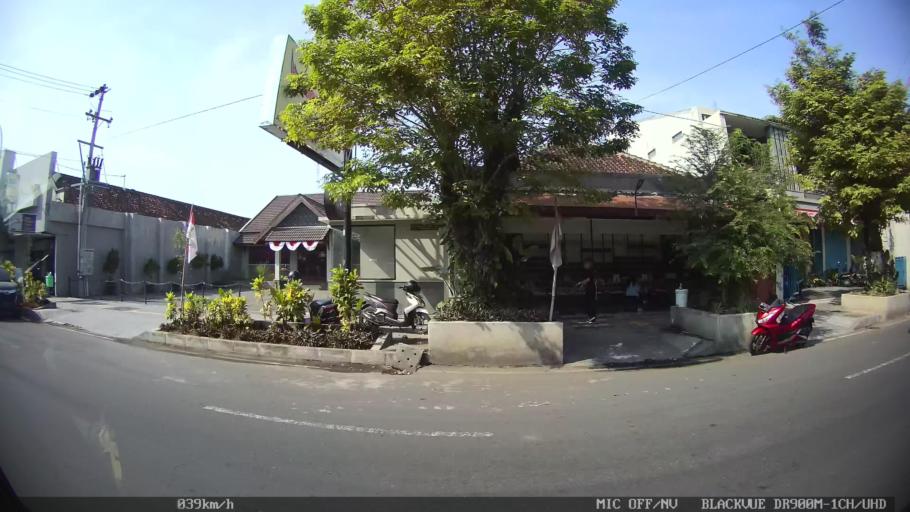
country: ID
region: Daerah Istimewa Yogyakarta
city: Yogyakarta
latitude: -7.8012
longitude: 110.3585
